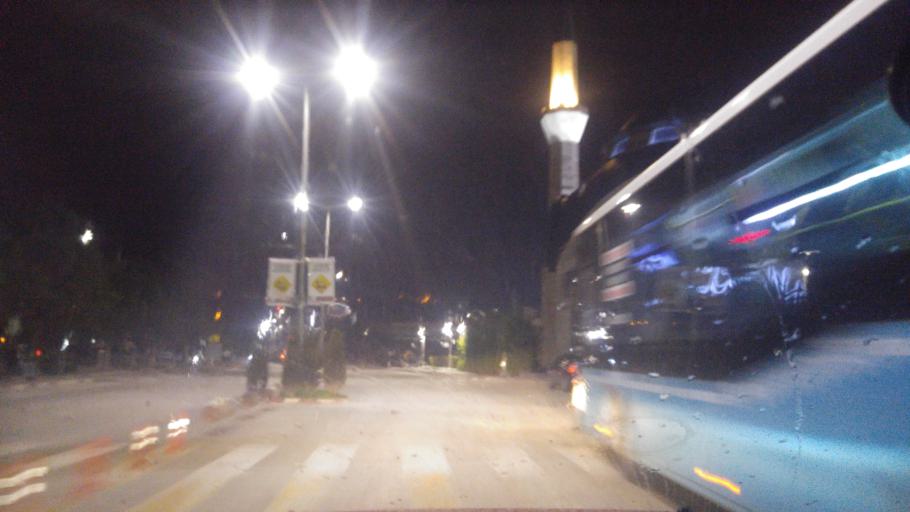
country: TR
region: Karabuk
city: Karabuk
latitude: 41.2113
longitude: 32.6550
